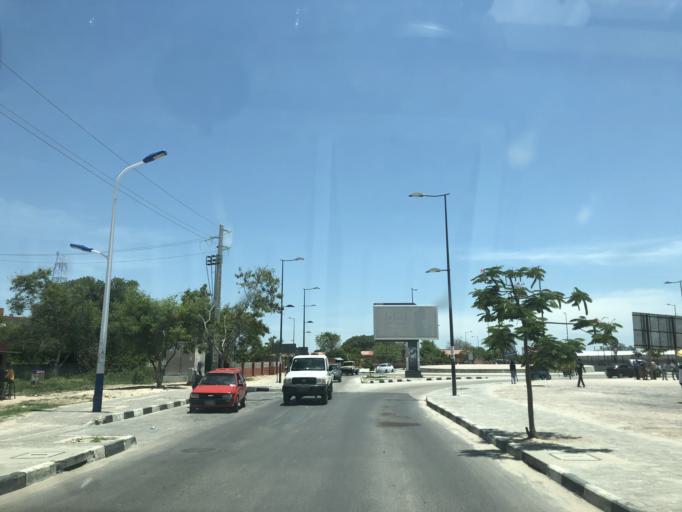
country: AO
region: Cunene
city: Ondjiva
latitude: -17.0671
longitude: 15.7298
